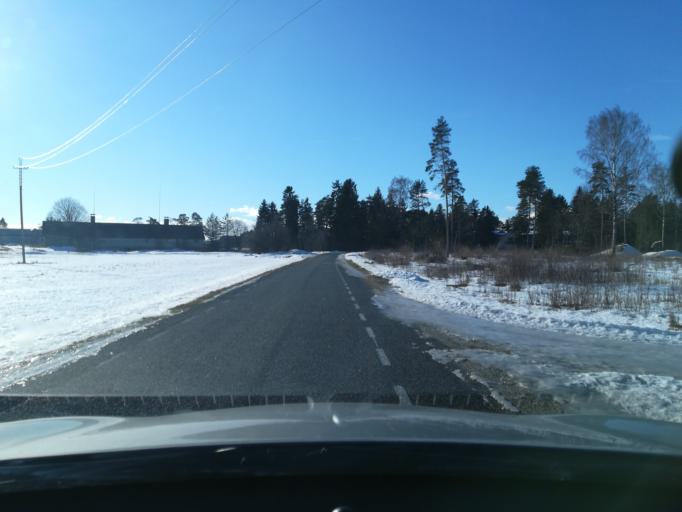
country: EE
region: Raplamaa
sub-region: Kohila vald
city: Kohila
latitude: 59.2295
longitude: 24.7573
